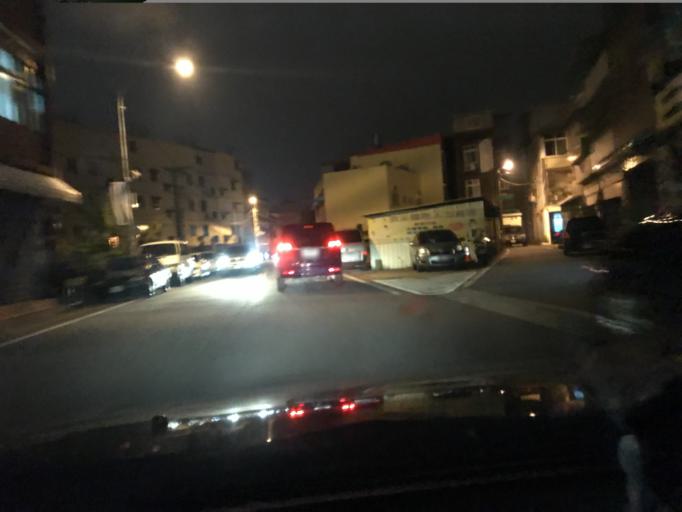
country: TW
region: Taiwan
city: Daxi
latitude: 24.8626
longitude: 121.2166
